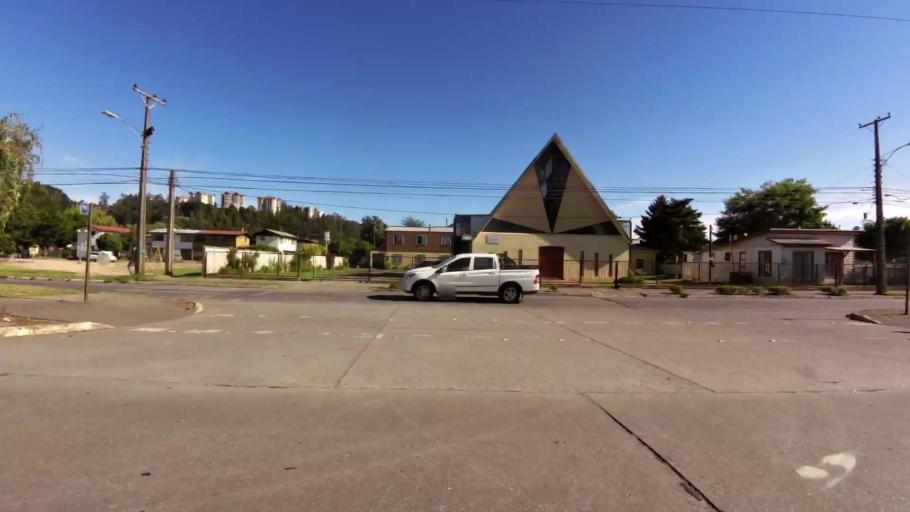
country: CL
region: Biobio
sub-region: Provincia de Concepcion
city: Concepcion
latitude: -36.8439
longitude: -73.1017
